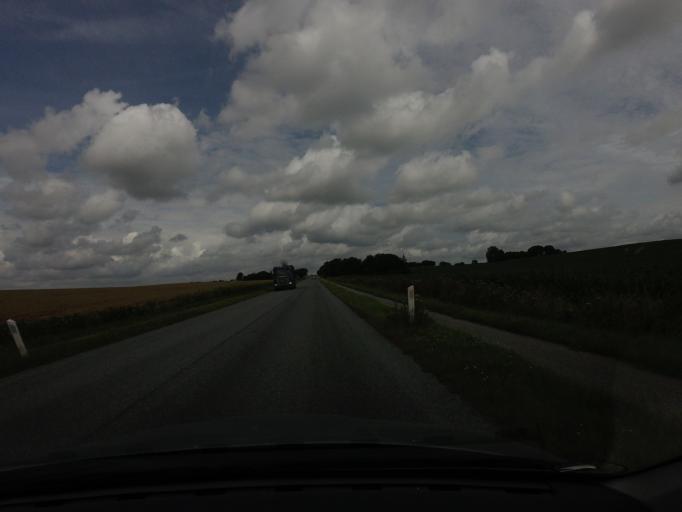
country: DK
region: North Denmark
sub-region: Hjorring Kommune
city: Tars
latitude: 57.3476
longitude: 10.2297
